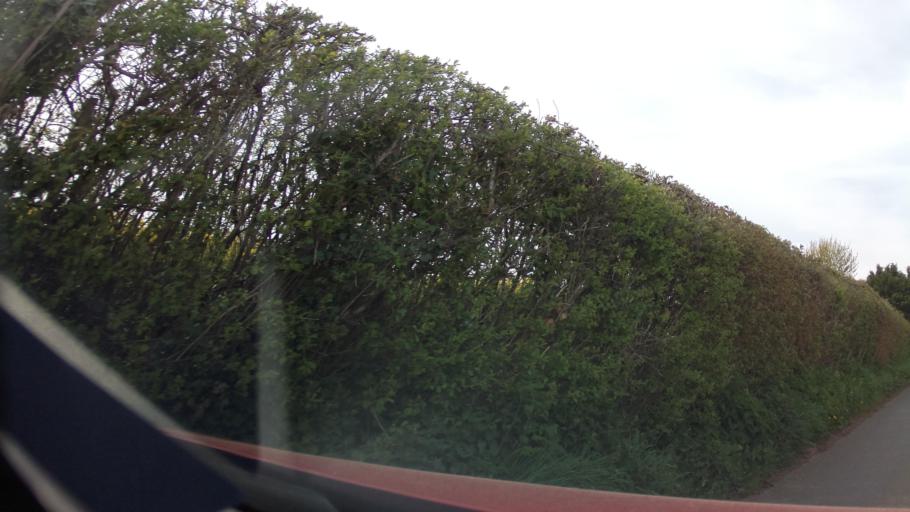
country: GB
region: England
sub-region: Dorset
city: Sherborne
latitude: 50.9876
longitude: -2.5159
